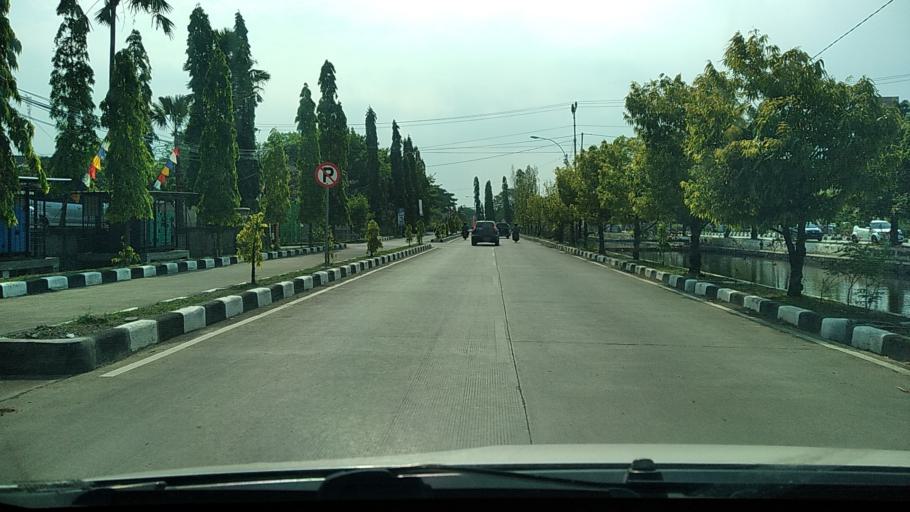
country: ID
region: Central Java
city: Semarang
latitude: -6.9623
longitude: 110.3925
